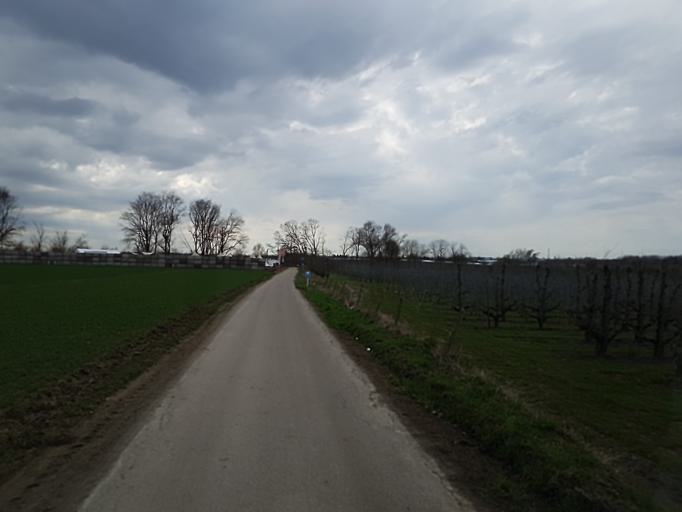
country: BE
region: Flanders
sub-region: Provincie Limburg
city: Sint-Truiden
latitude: 50.8151
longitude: 5.2574
